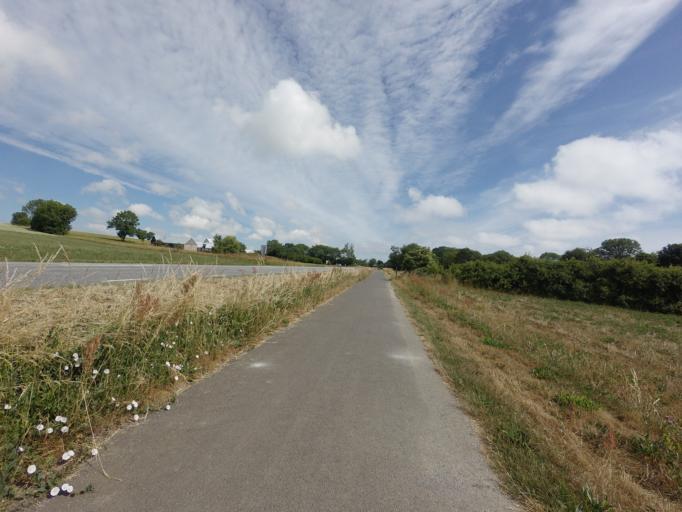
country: SE
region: Skane
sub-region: Simrishamns Kommun
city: Simrishamn
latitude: 55.4958
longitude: 14.3160
